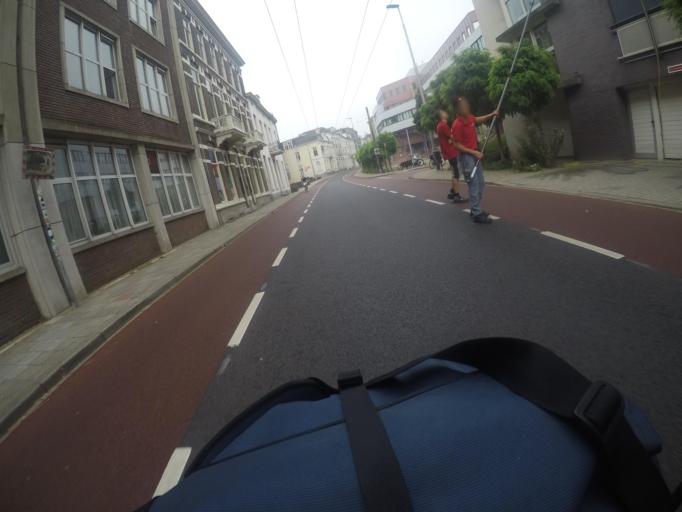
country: NL
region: Gelderland
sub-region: Gemeente Arnhem
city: Burgemeesterswijk
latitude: 51.9832
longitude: 5.8979
